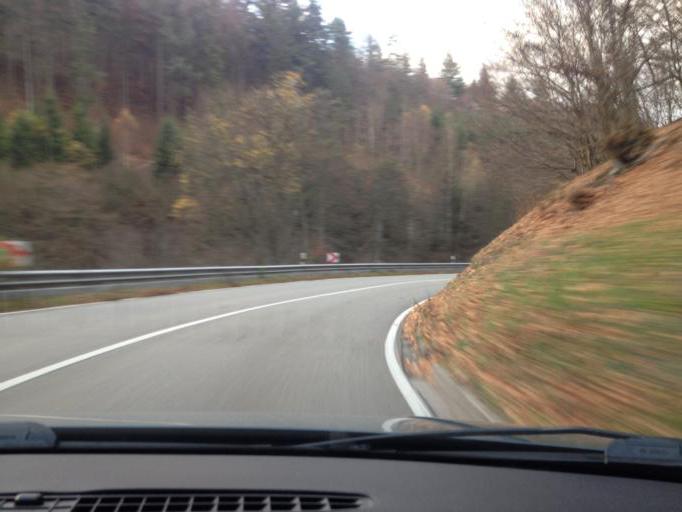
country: DE
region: Rheinland-Pfalz
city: Weidenthal
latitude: 49.4091
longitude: 8.0065
